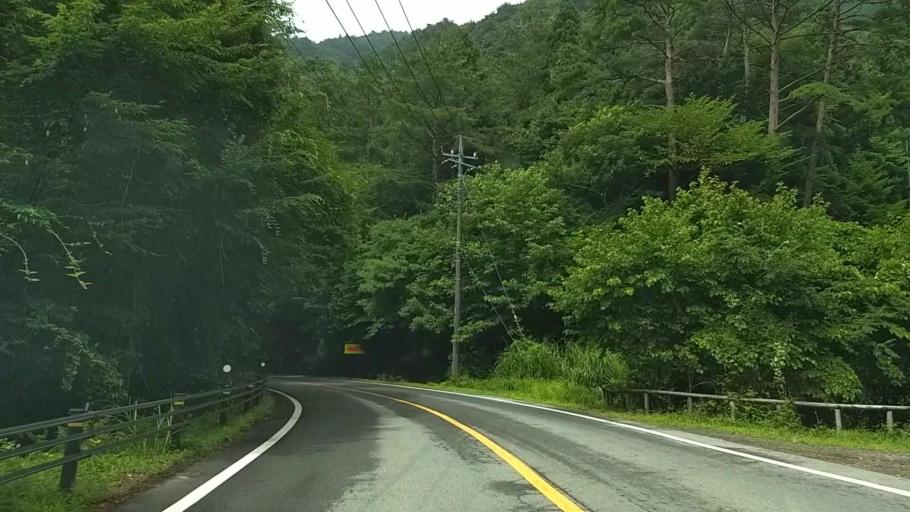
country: JP
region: Yamanashi
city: Fujikawaguchiko
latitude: 35.4764
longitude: 138.5941
